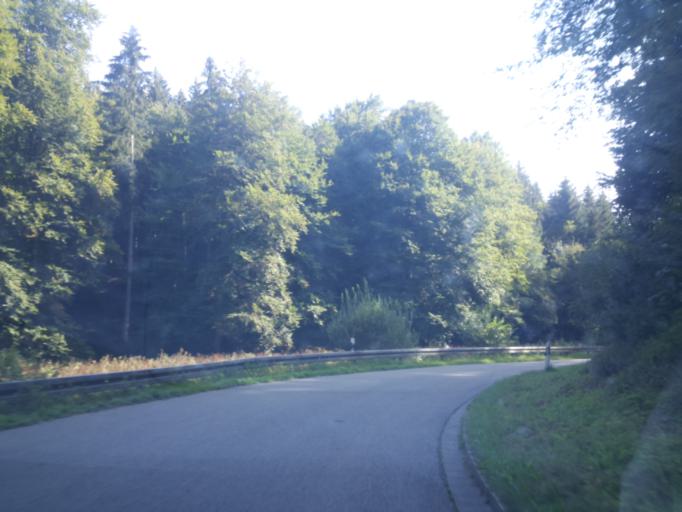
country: DE
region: Bavaria
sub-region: Upper Bavaria
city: Denkendorf
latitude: 48.9222
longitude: 11.4062
